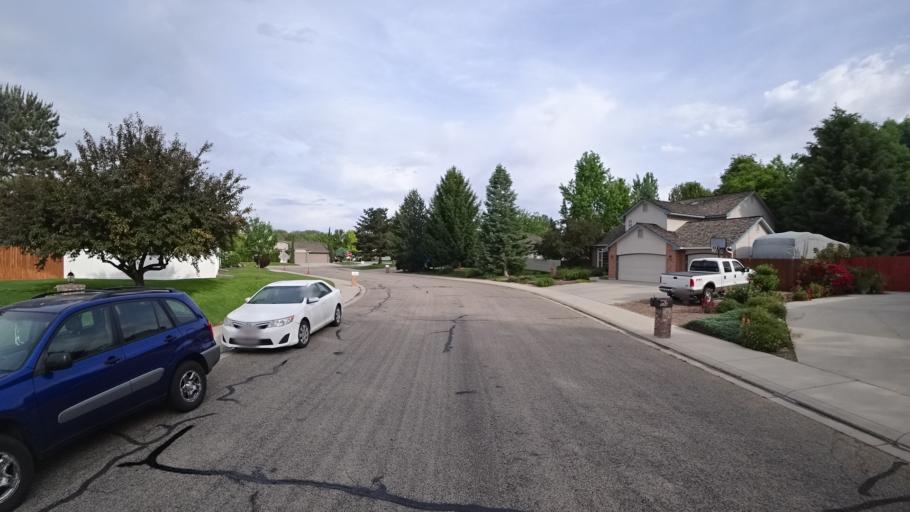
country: US
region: Idaho
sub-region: Ada County
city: Meridian
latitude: 43.5859
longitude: -116.3881
